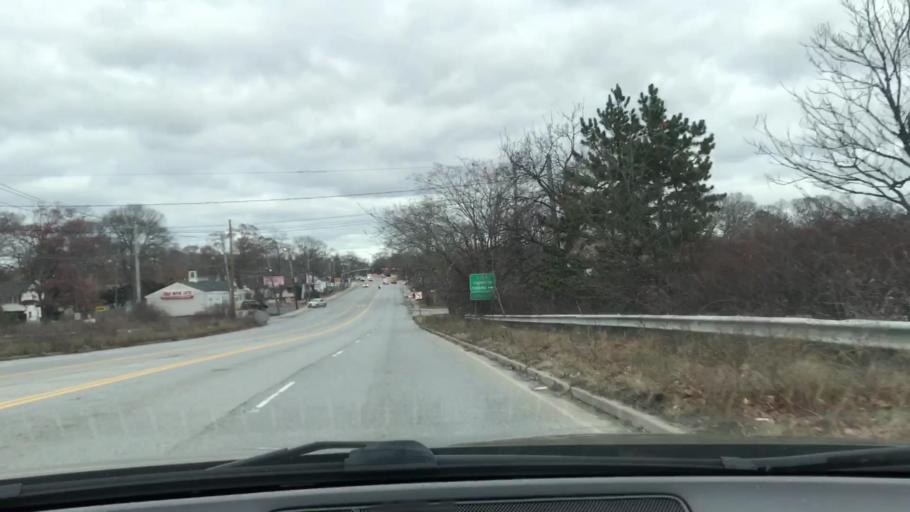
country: US
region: New York
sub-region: Suffolk County
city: Ronkonkoma
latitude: 40.8087
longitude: -73.1112
